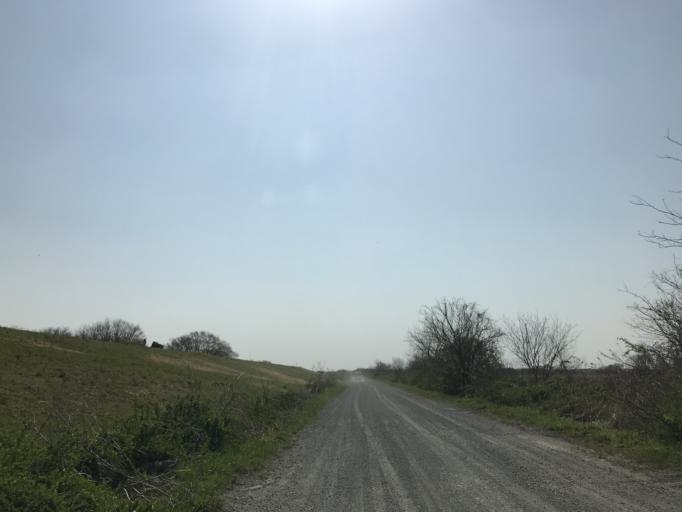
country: JP
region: Ibaraki
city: Moriya
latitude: 35.9201
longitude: 139.9835
